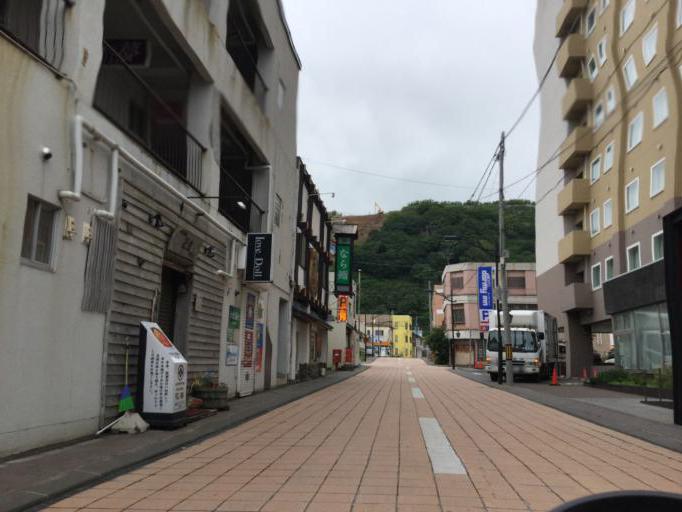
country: JP
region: Hokkaido
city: Wakkanai
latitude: 45.4183
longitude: 141.6753
